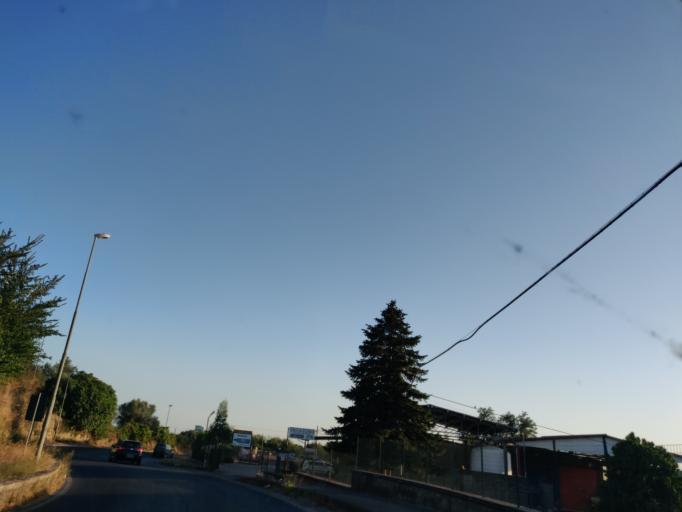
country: IT
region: Latium
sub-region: Provincia di Viterbo
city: Canino
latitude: 42.4602
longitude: 11.7430
